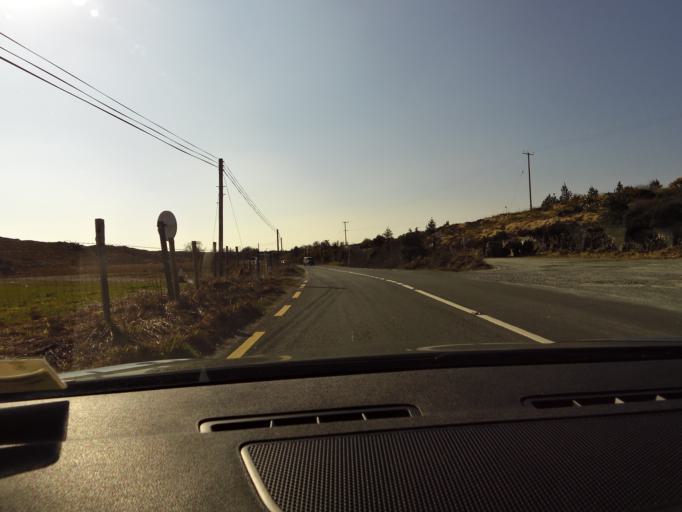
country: IE
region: Connaught
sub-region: County Galway
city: Clifden
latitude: 53.4777
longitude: -9.9055
